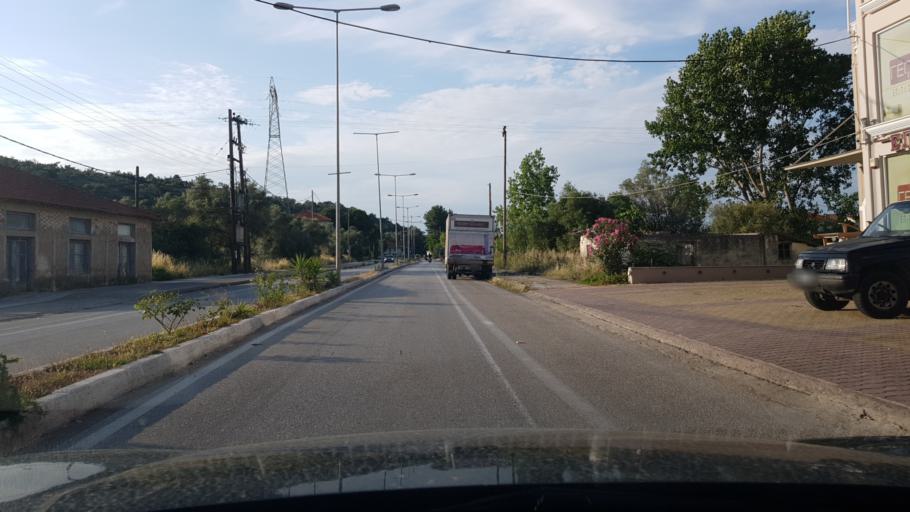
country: GR
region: Ionian Islands
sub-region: Lefkada
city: Lefkada
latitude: 38.8023
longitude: 20.7154
